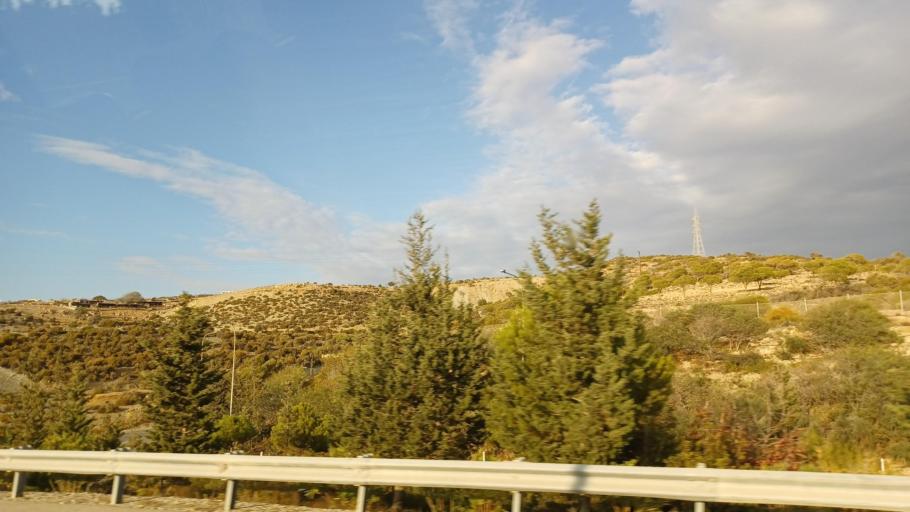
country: CY
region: Limassol
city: Pissouri
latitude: 34.6707
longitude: 32.6138
